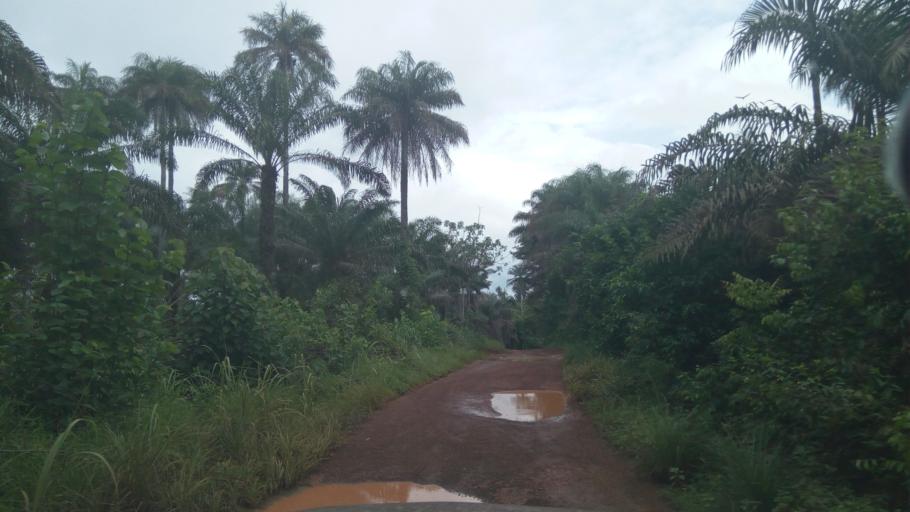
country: SL
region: Southern Province
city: Bomi
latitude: 7.3157
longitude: -11.6084
